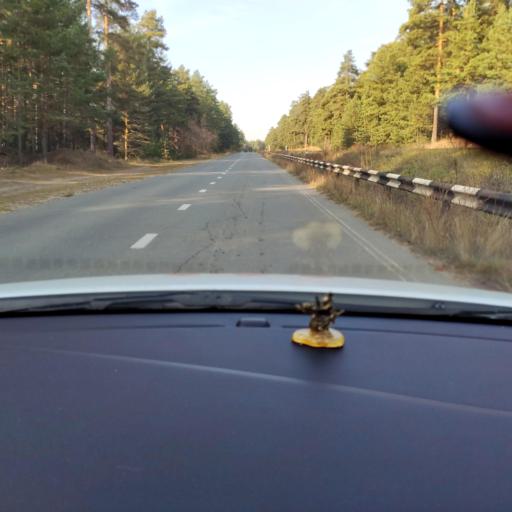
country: RU
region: Tatarstan
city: Osinovo
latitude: 55.8245
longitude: 48.9102
